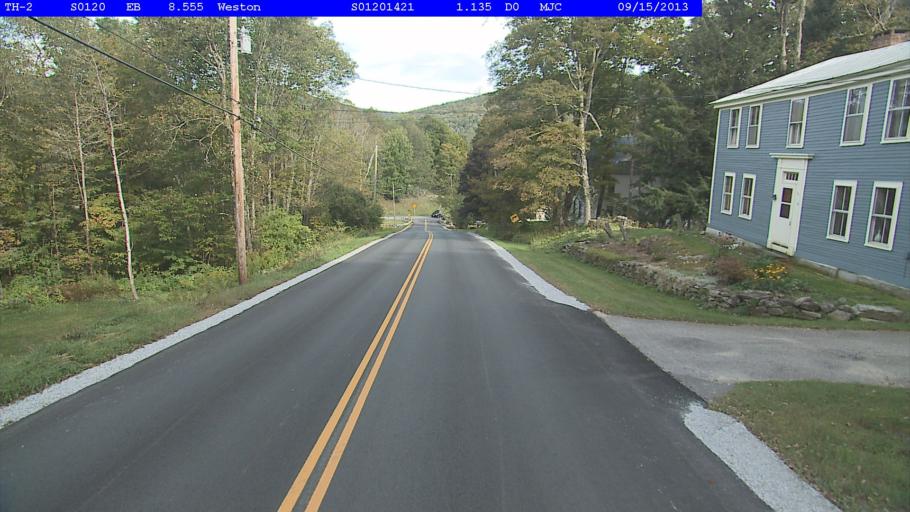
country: US
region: Vermont
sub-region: Windsor County
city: Chester
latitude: 43.2933
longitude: -72.7986
